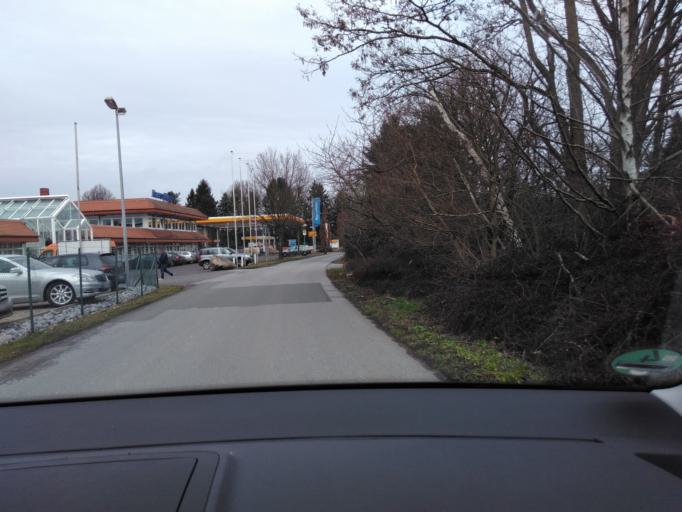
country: DE
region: North Rhine-Westphalia
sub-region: Regierungsbezirk Detmold
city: Verl
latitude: 51.8777
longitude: 8.4864
